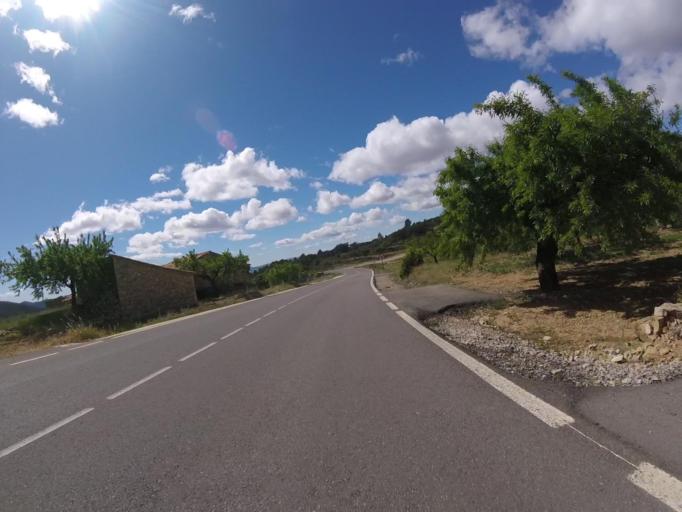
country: ES
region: Valencia
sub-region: Provincia de Castello
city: Culla
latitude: 40.2985
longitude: -0.1191
